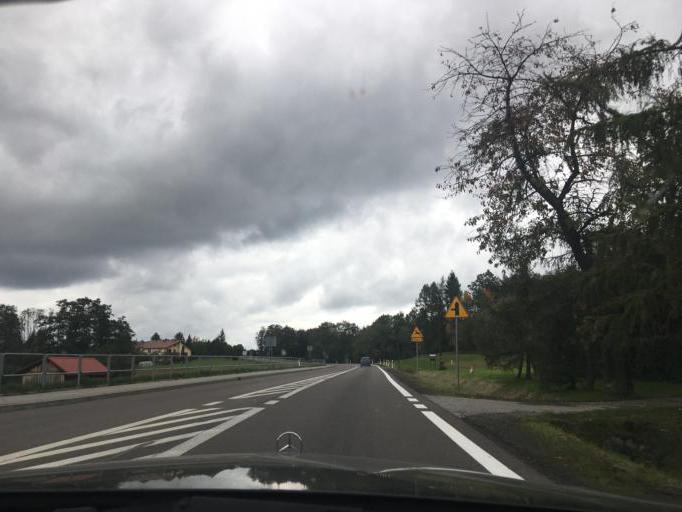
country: PL
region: Subcarpathian Voivodeship
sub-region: Powiat brzozowski
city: Jablonica Polska
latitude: 49.7188
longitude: 21.9009
